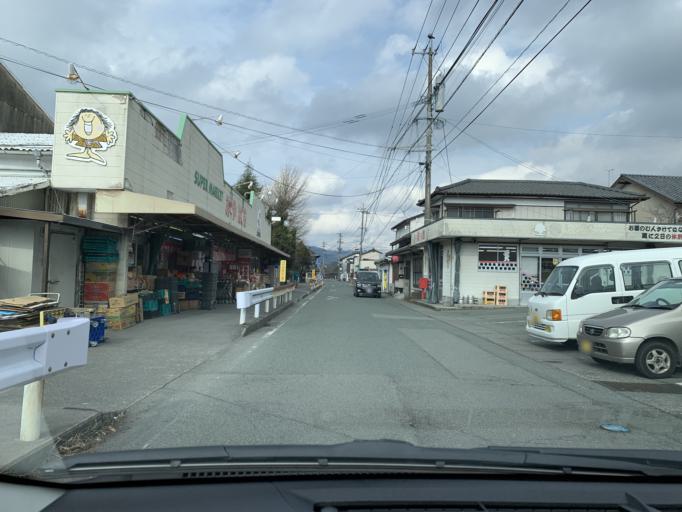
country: JP
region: Kumamoto
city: Aso
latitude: 32.9453
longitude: 131.1163
